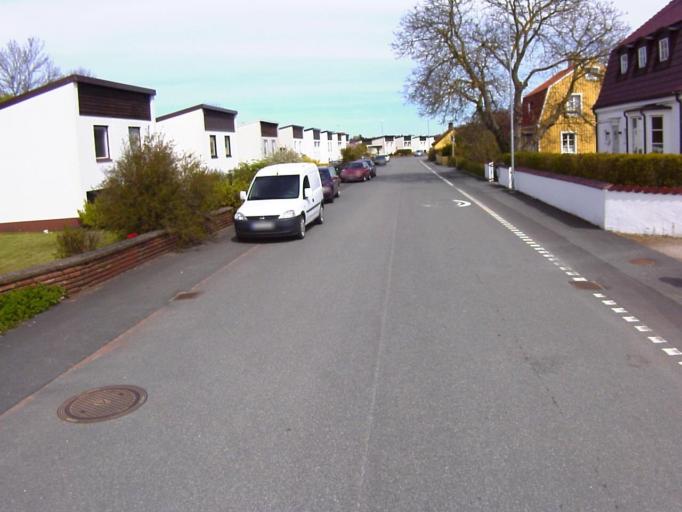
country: SE
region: Skane
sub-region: Kristianstads Kommun
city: Kristianstad
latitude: 56.0454
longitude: 14.1525
